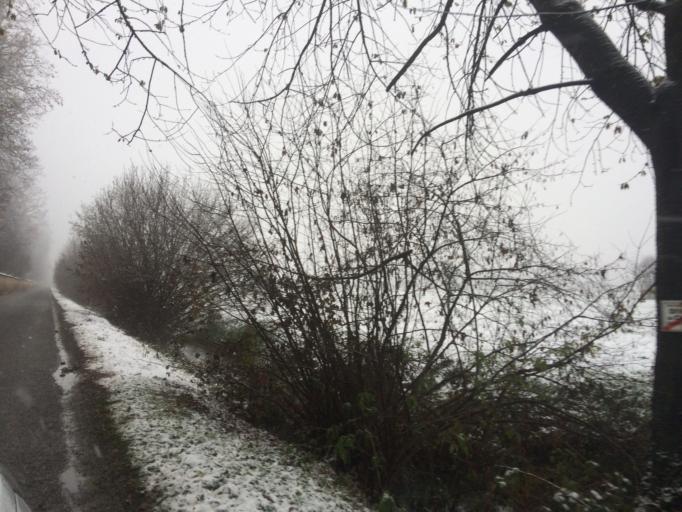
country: IT
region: Piedmont
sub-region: Provincia di Cuneo
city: Racconigi
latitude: 44.7787
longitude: 7.6688
